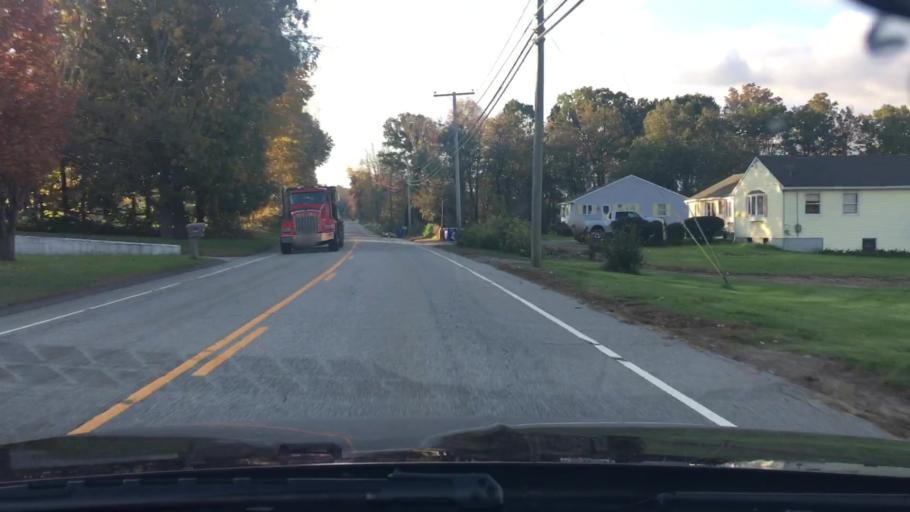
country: US
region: Connecticut
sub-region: Tolland County
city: Tolland
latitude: 41.8788
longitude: -72.4050
